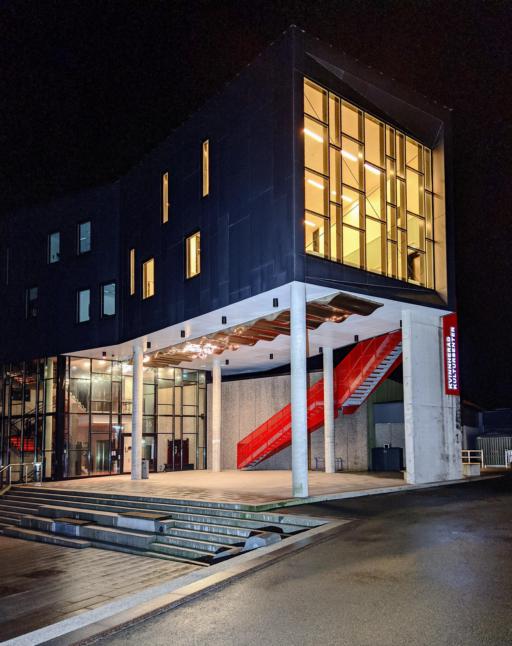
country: NO
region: Rogaland
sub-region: Vindafjord
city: Olen
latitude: 59.8611
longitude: 5.7560
